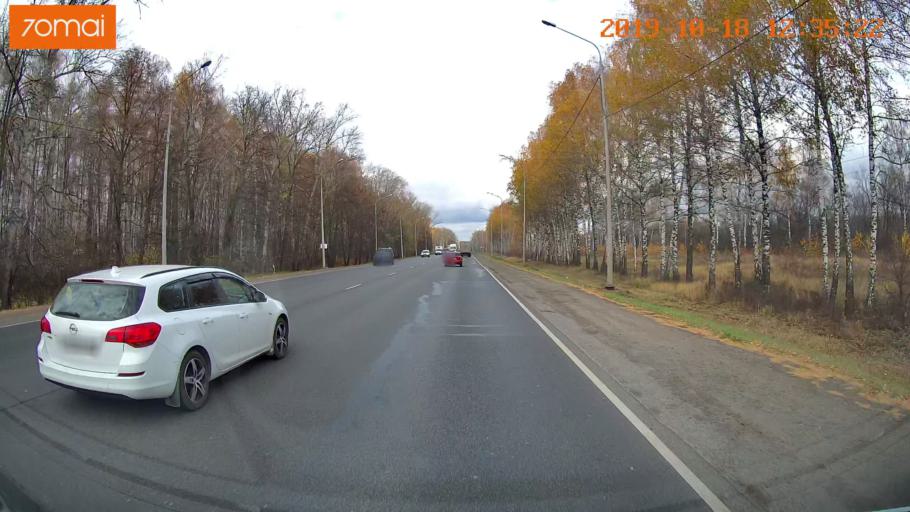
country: RU
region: Rjazan
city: Ryazan'
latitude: 54.6236
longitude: 39.6359
